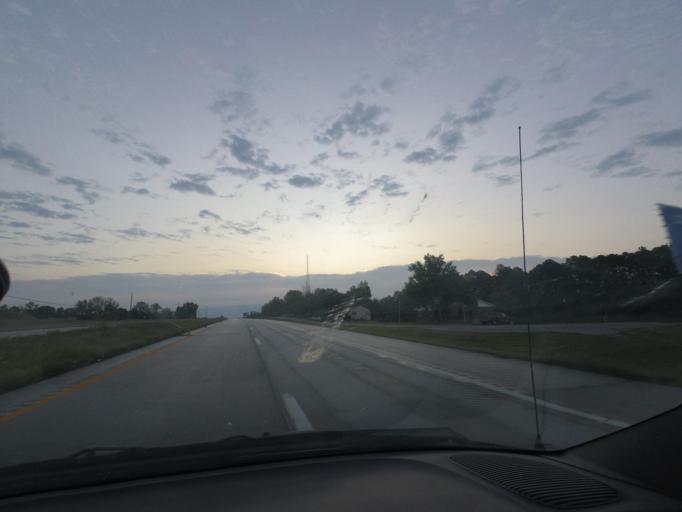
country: US
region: Missouri
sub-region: Macon County
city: Macon
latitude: 39.7493
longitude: -92.4815
